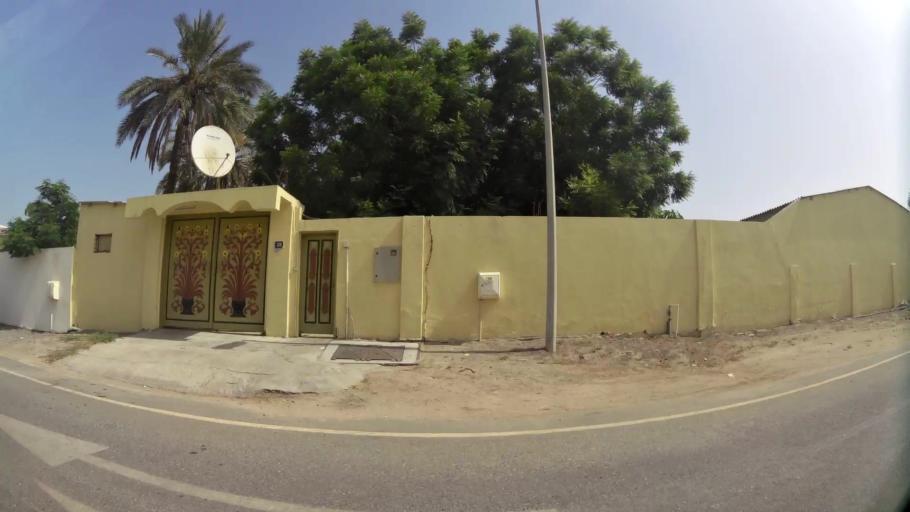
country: AE
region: Ash Shariqah
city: Sharjah
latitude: 25.3536
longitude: 55.4177
